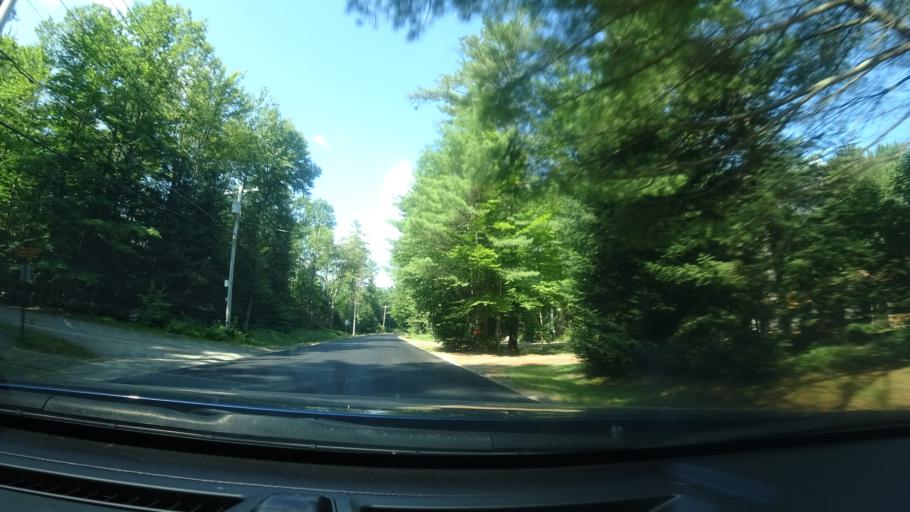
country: US
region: New York
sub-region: Warren County
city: Warrensburg
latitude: 43.6526
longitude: -73.8267
